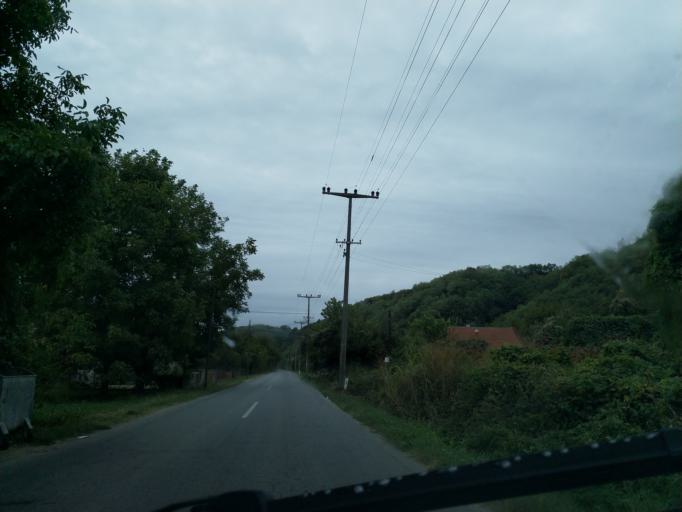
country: RS
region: Central Serbia
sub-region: Sumadijski Okrug
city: Batocina
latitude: 44.0997
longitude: 21.1635
